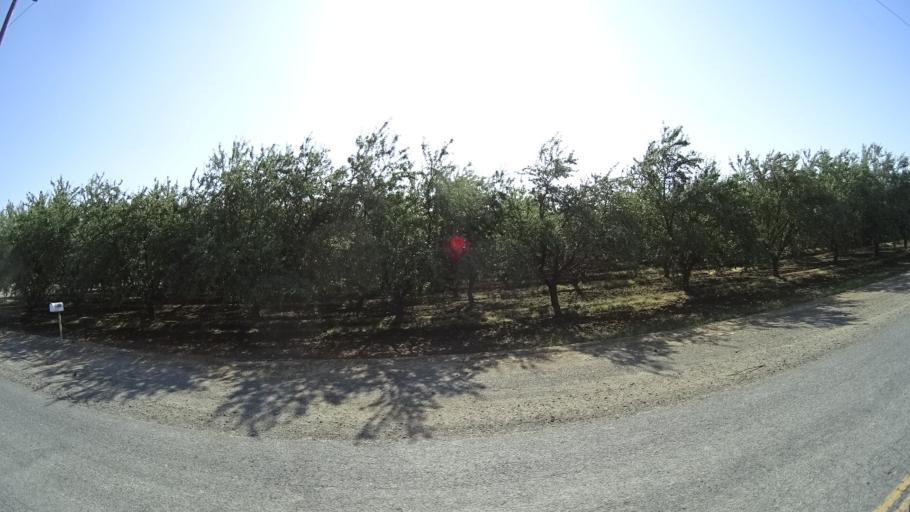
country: US
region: California
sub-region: Kings County
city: Home Garden
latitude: 36.2836
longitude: -119.5831
